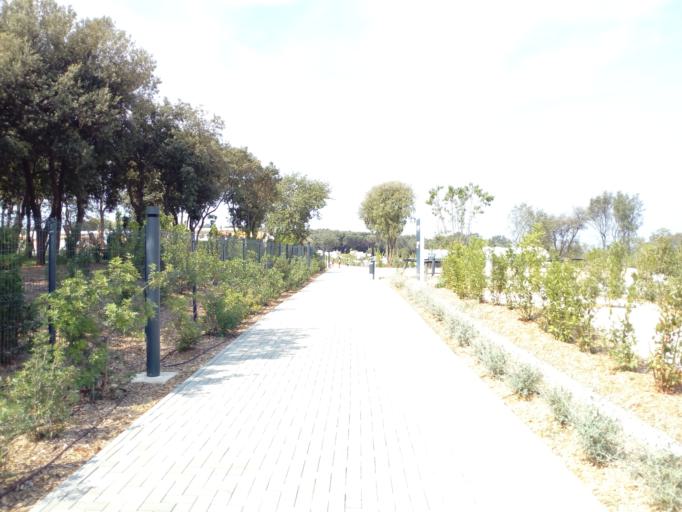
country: HR
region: Istarska
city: Vrsar
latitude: 45.1747
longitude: 13.5970
